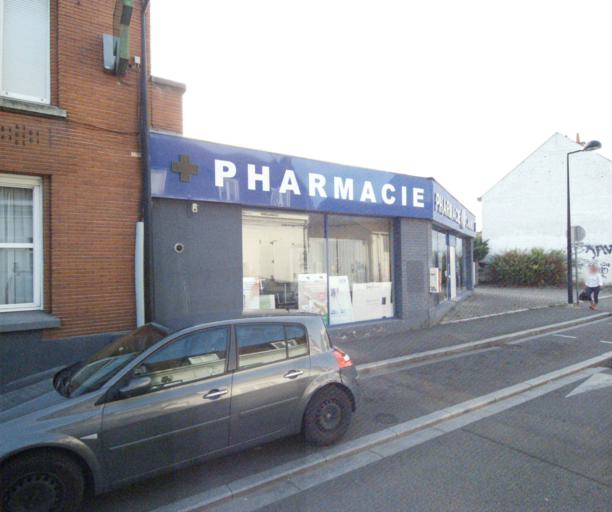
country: FR
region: Nord-Pas-de-Calais
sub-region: Departement du Nord
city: Faches-Thumesnil
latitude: 50.6019
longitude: 3.0677
